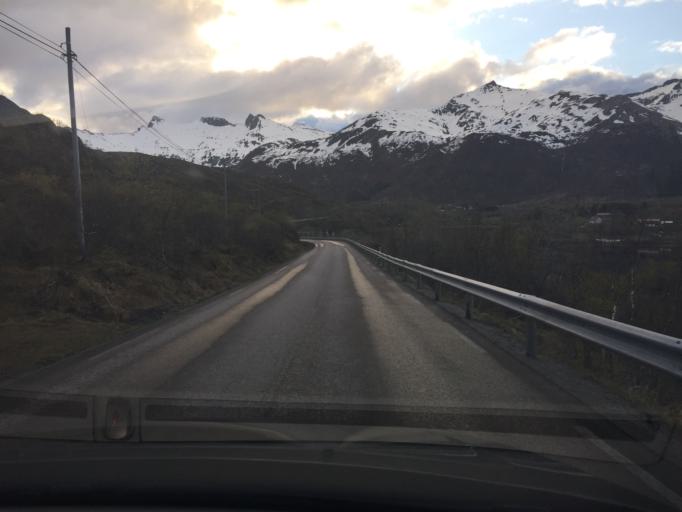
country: NO
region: Nordland
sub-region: Vagan
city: Svolvaer
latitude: 68.3169
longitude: 14.7128
